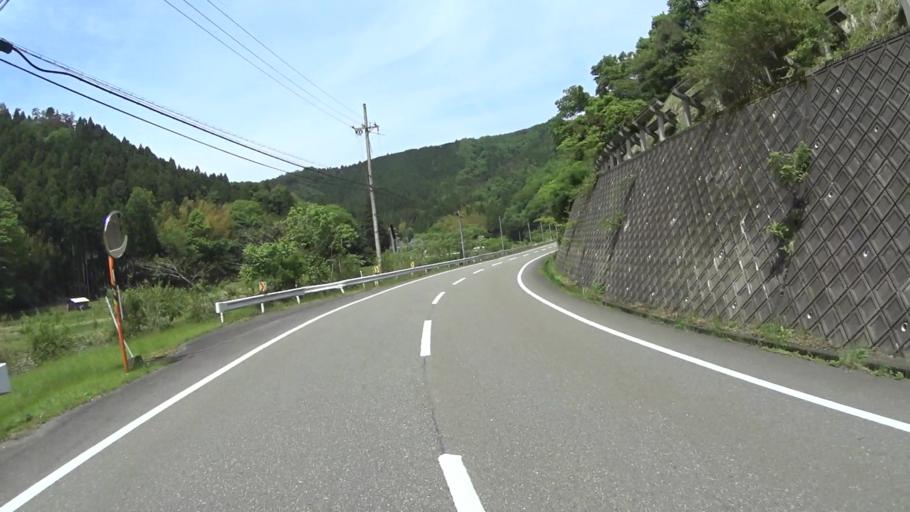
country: JP
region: Kyoto
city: Maizuru
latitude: 35.4043
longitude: 135.4635
